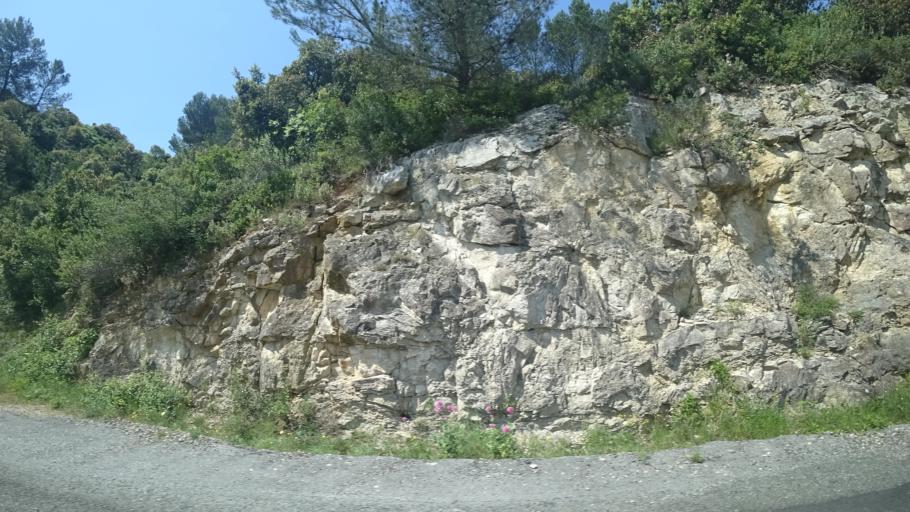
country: FR
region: Languedoc-Roussillon
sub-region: Departement de l'Herault
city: Olonzac
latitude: 43.3494
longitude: 2.7487
